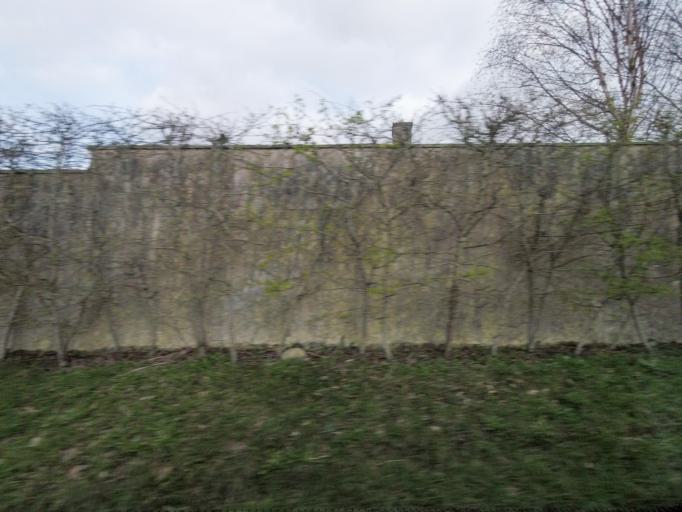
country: IE
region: Leinster
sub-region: Kildare
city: Naas
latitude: 53.2001
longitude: -6.6532
